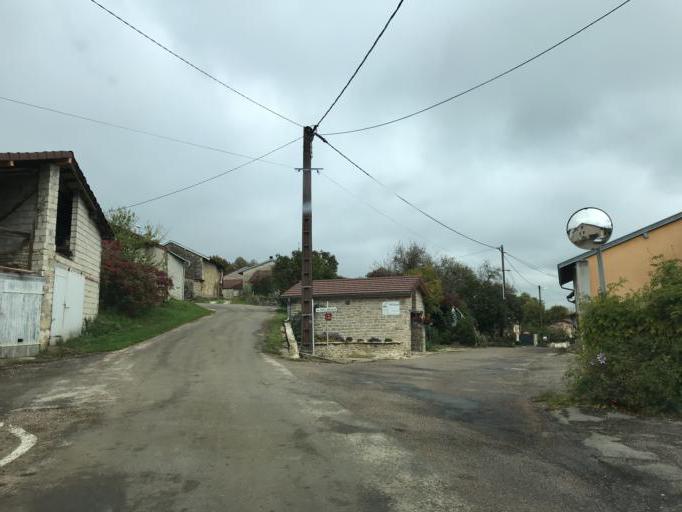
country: FR
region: Franche-Comte
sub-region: Departement du Jura
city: Arinthod
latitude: 46.4459
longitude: 5.5290
